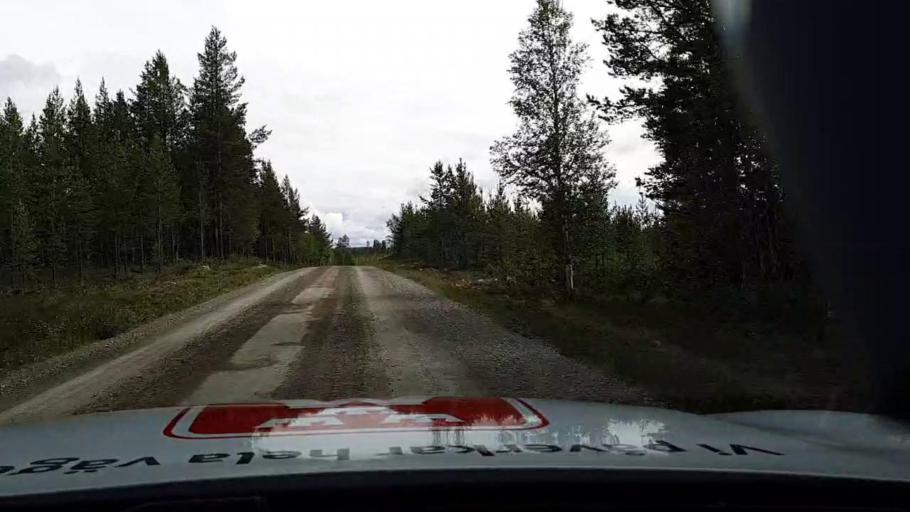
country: SE
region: Jaemtland
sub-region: Are Kommun
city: Jarpen
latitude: 62.5109
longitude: 13.4922
